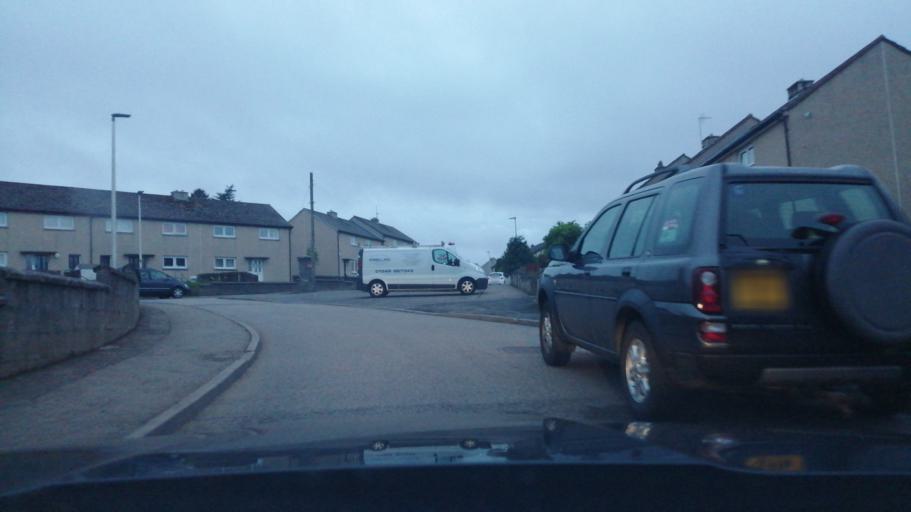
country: GB
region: Scotland
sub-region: Moray
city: Keith
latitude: 57.5408
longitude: -2.9562
